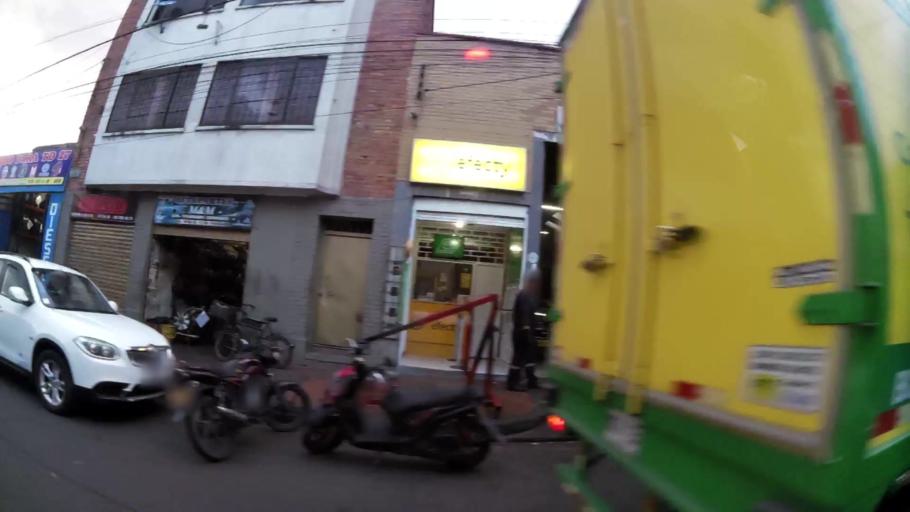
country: CO
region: Bogota D.C.
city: Bogota
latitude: 4.6028
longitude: -74.0877
